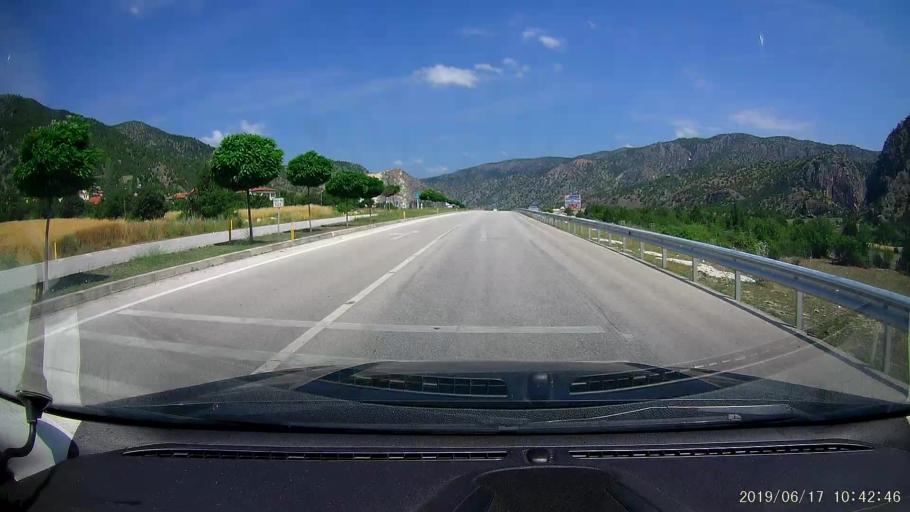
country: TR
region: Corum
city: Hacihamza
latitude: 41.0523
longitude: 34.5471
